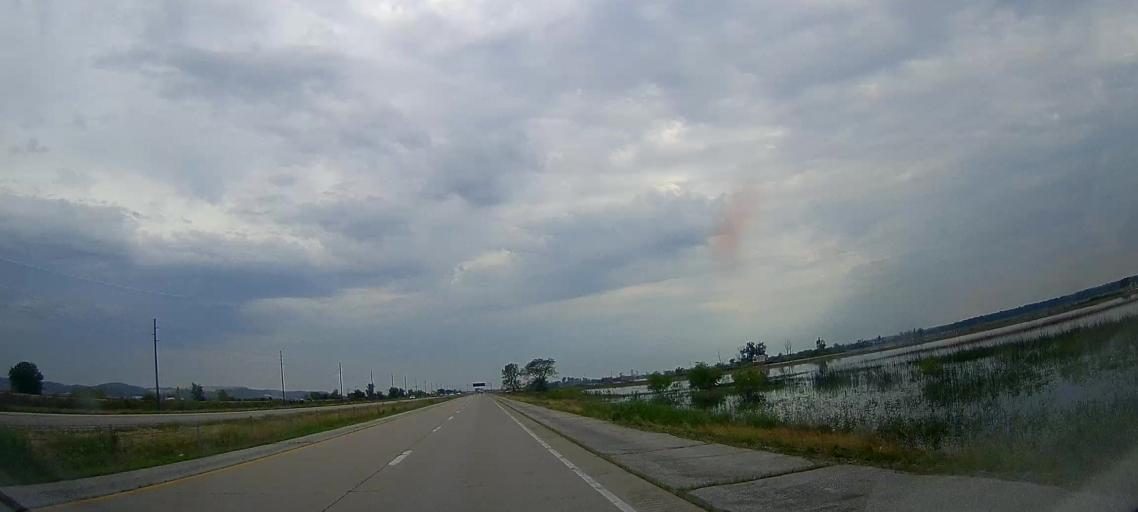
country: US
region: Iowa
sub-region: Pottawattamie County
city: Carter Lake
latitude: 41.3879
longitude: -95.8997
